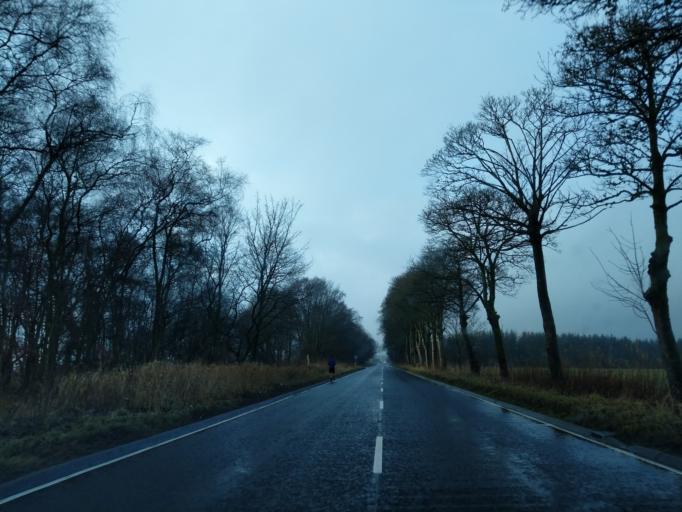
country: GB
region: Scotland
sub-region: Perth and Kinross
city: Kinross
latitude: 56.2023
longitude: -3.4877
